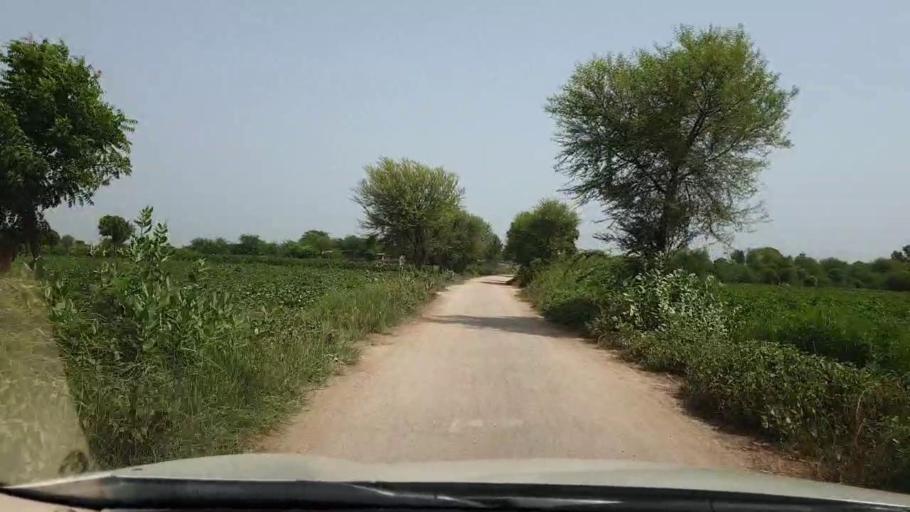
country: PK
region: Sindh
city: Tando Ghulam Ali
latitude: 25.2316
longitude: 68.9160
